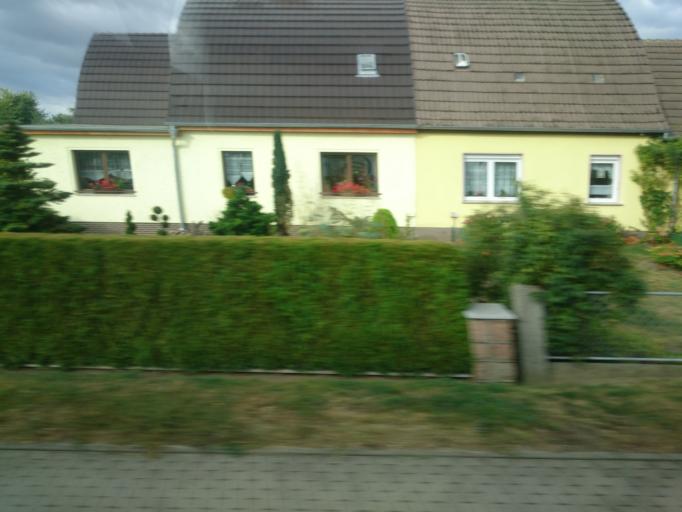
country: DE
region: Mecklenburg-Vorpommern
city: Pasewalk
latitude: 53.5204
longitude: 13.9770
